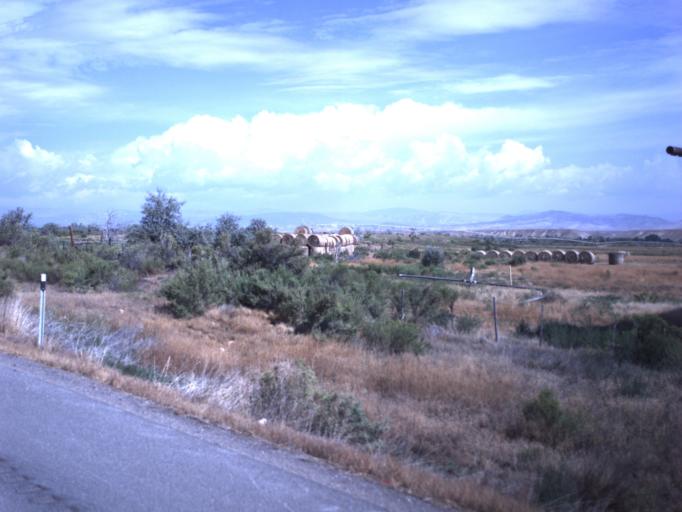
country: US
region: Utah
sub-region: Uintah County
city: Naples
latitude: 40.3821
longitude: -109.4242
